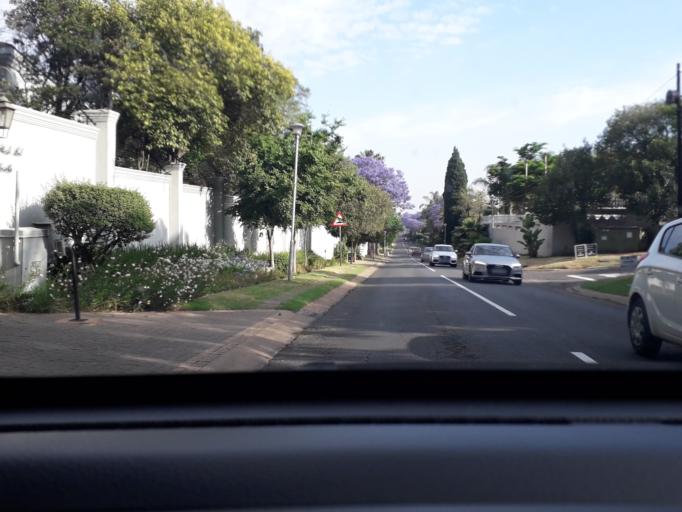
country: ZA
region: Gauteng
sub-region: City of Johannesburg Metropolitan Municipality
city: Modderfontein
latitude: -26.0759
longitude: 28.0567
